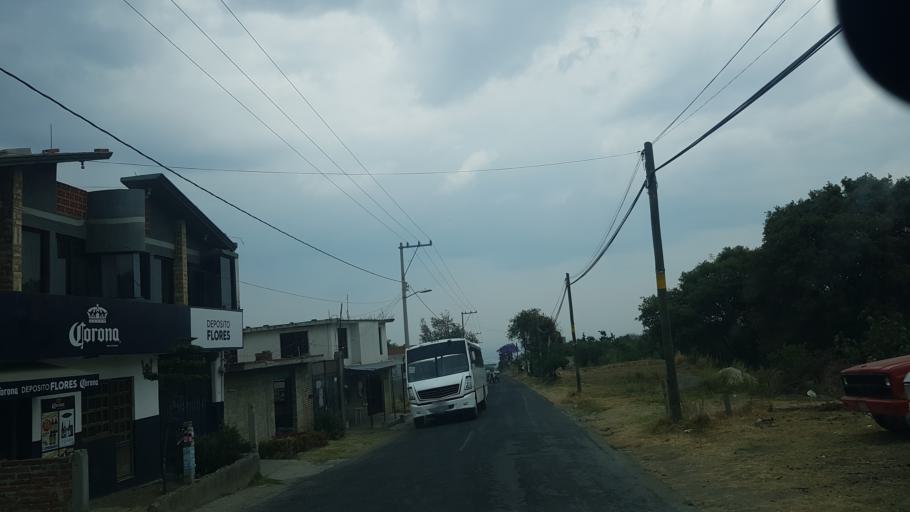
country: MX
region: Puebla
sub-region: Chiautzingo
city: San Nicolas Zecalacoayan
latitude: 19.1787
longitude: -98.4870
